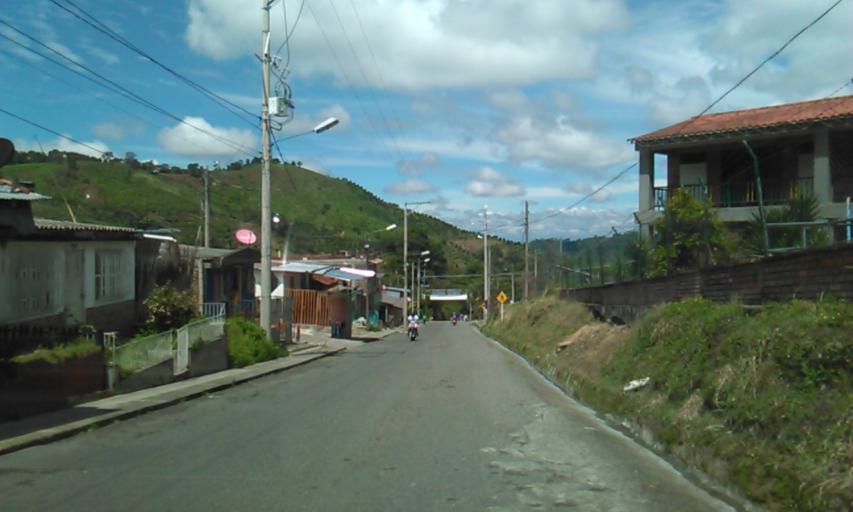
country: CO
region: Quindio
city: Cordoba
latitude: 4.3936
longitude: -75.6877
